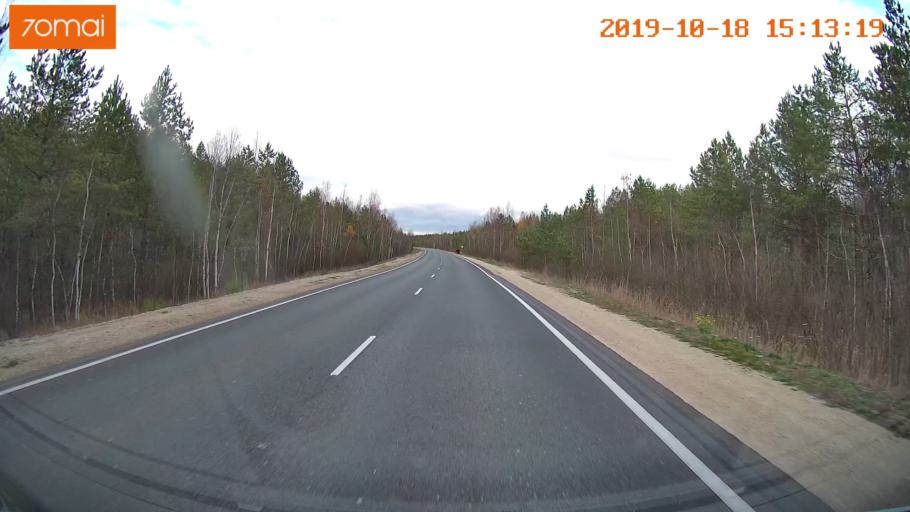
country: RU
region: Vladimir
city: Gus'-Khrustal'nyy
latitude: 55.5853
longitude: 40.7153
